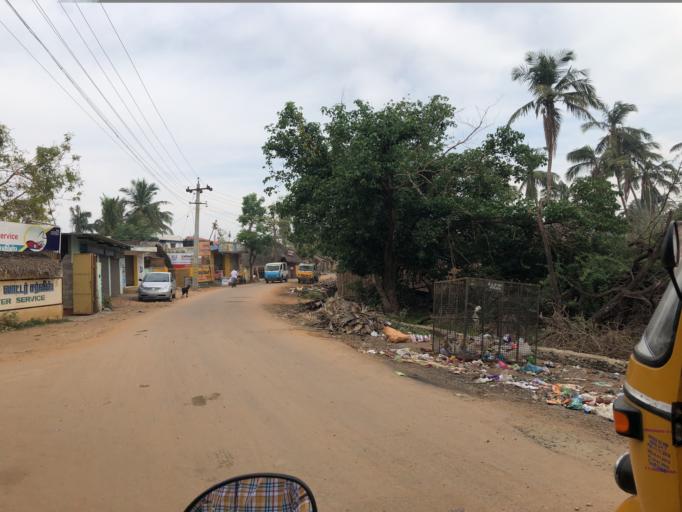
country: IN
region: Tamil Nadu
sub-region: Thanjavur
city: Adirampattinam
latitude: 10.3383
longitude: 79.3799
